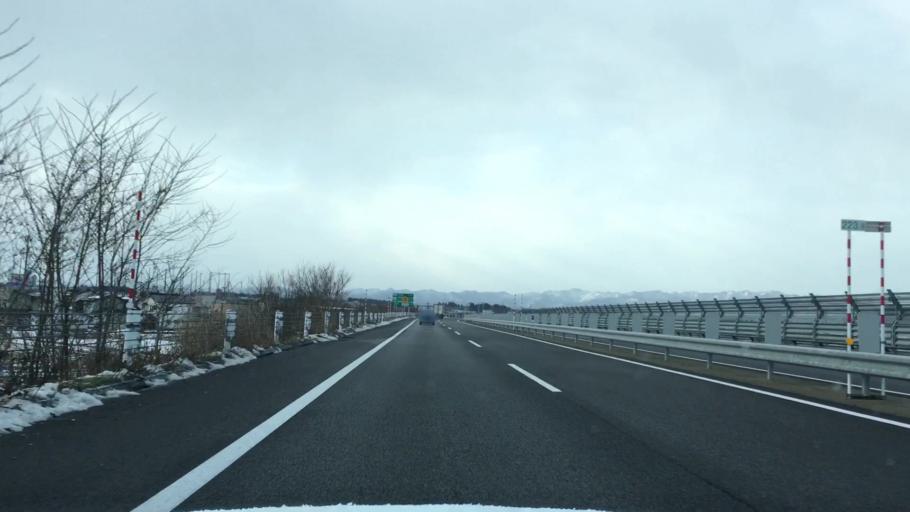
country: JP
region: Akita
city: Odate
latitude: 40.2956
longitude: 140.5536
